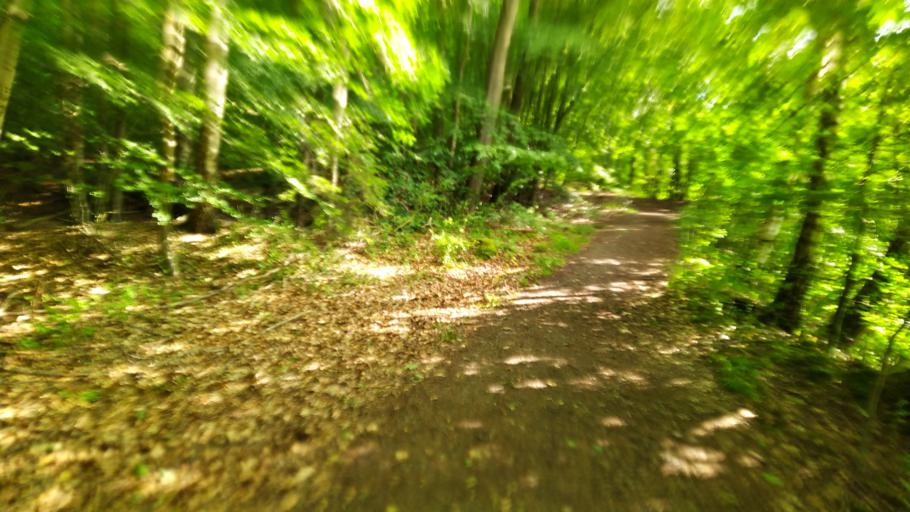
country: DE
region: Lower Saxony
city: Deinstedt
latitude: 53.4397
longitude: 9.1898
